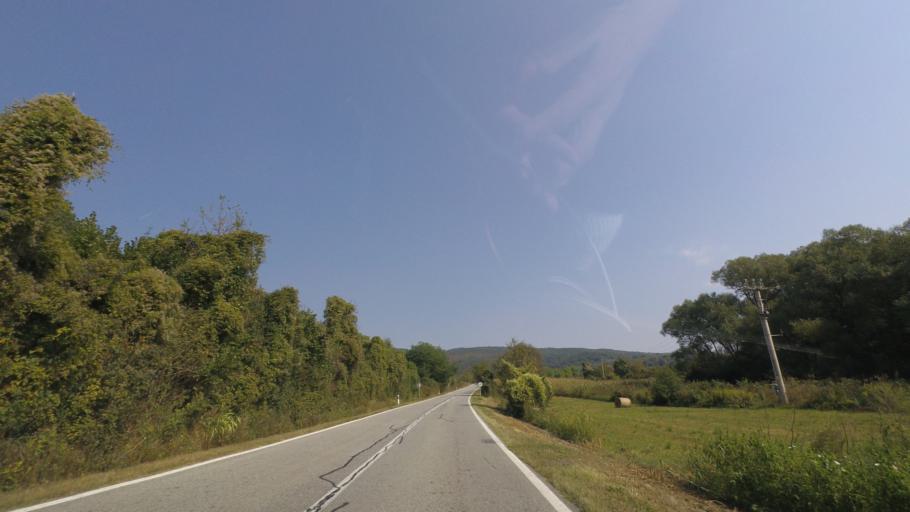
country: HR
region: Pozesko-Slavonska
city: Velika
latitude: 45.4174
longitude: 17.5020
